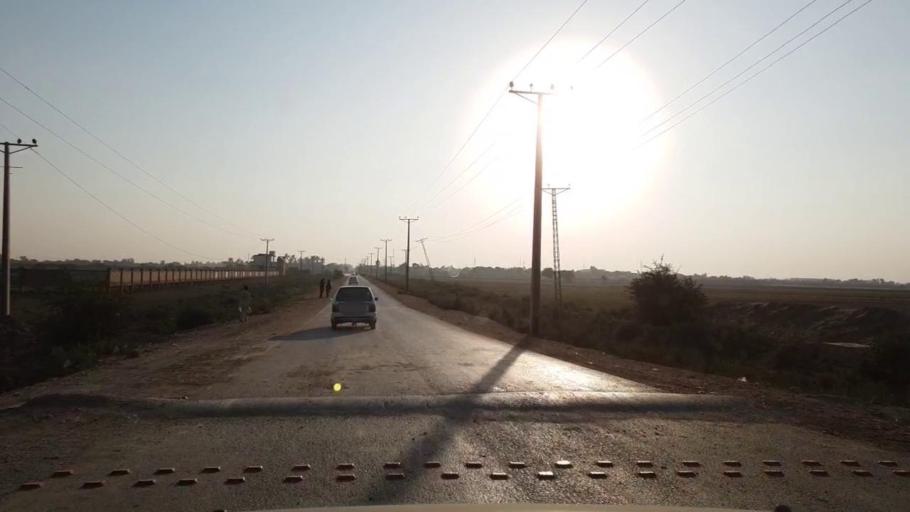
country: PK
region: Sindh
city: Daro Mehar
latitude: 24.6141
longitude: 68.0894
